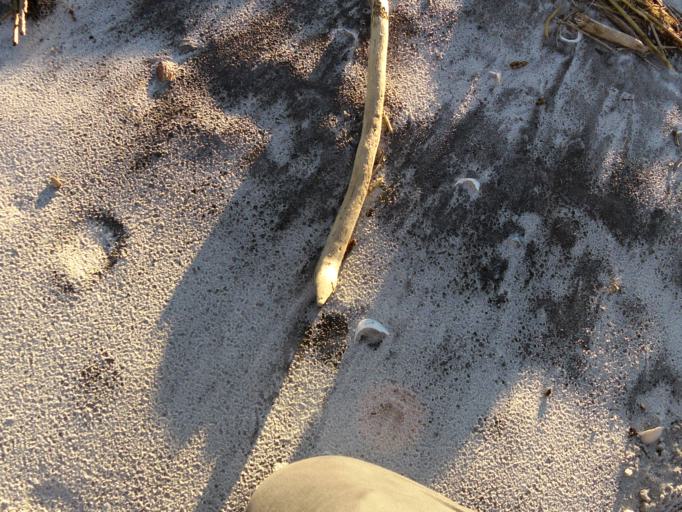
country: US
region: Florida
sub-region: Duval County
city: Atlantic Beach
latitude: 30.4693
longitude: -81.4127
